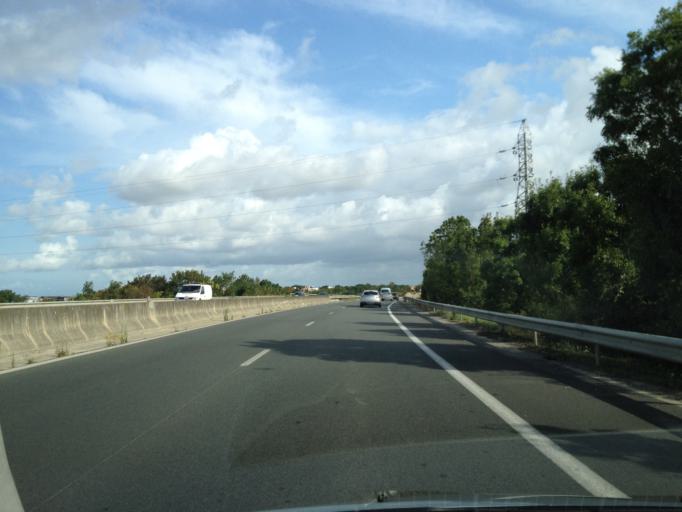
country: FR
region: Poitou-Charentes
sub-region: Departement de la Charente-Maritime
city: Perigny
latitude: 46.1606
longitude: -1.1212
